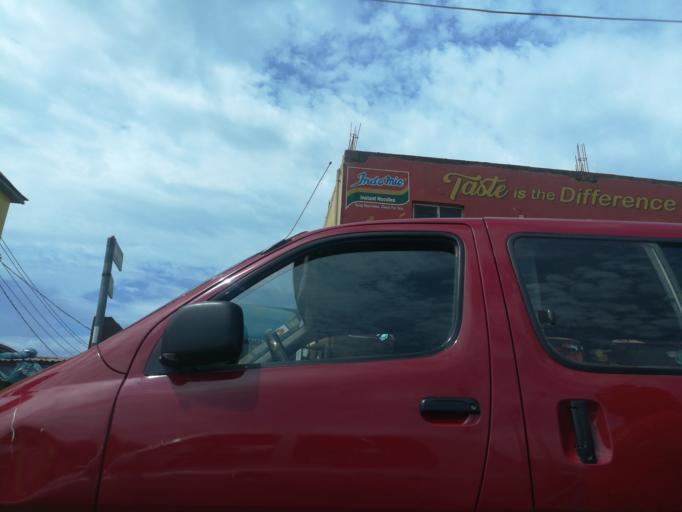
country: NG
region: Lagos
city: Agege
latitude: 6.6221
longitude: 3.3271
